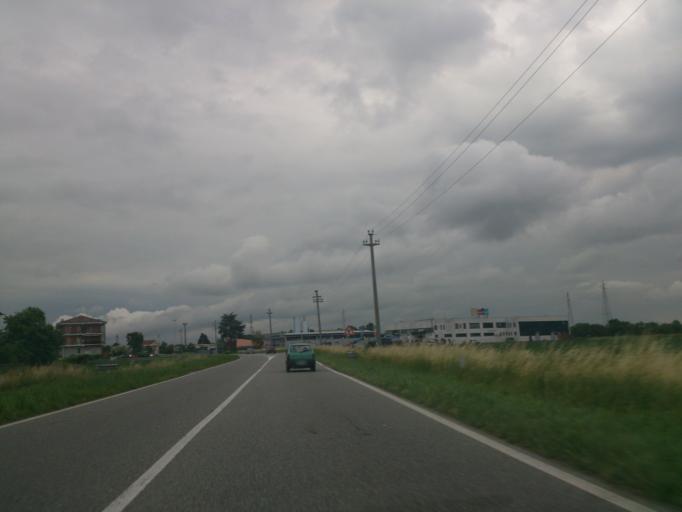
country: IT
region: Lombardy
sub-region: Citta metropolitana di Milano
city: Triginto
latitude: 45.4023
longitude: 9.3208
